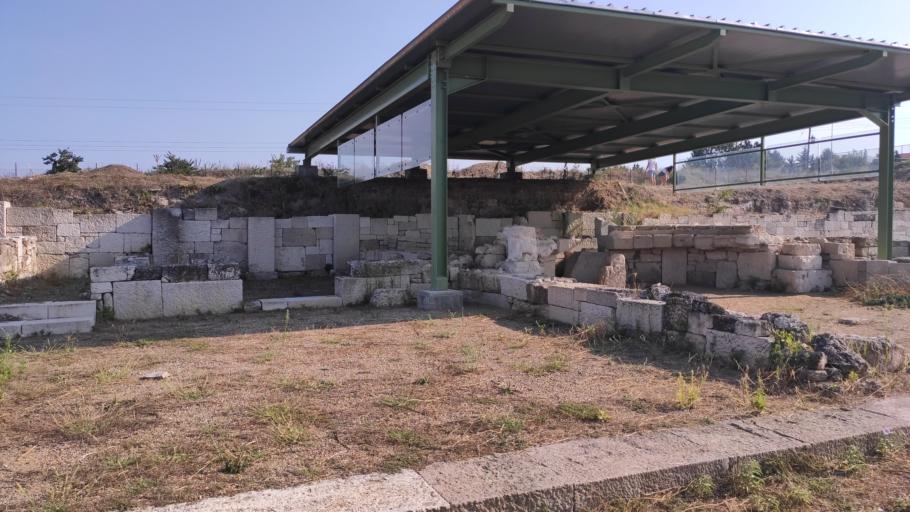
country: GR
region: Central Macedonia
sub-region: Nomos Pellis
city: Pella
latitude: 40.7568
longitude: 22.5198
